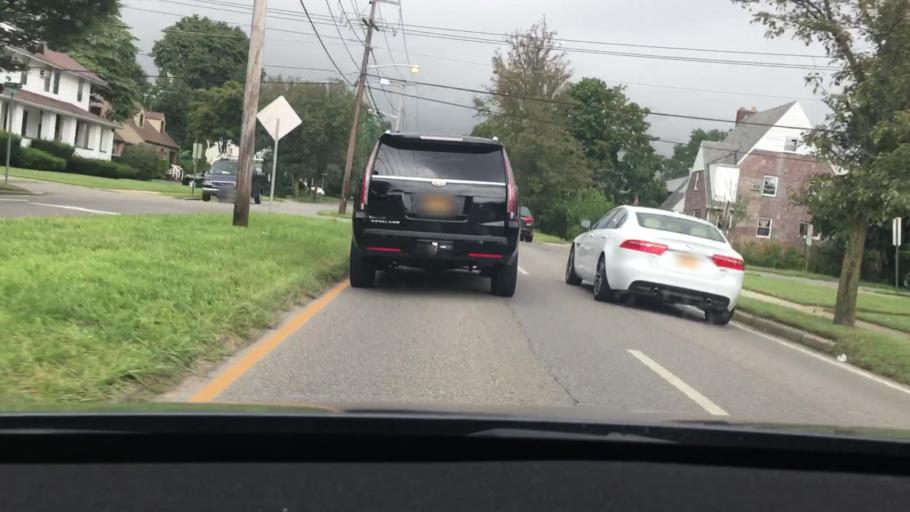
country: US
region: New York
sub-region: Nassau County
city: Garden City Park
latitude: 40.7378
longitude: -73.6616
